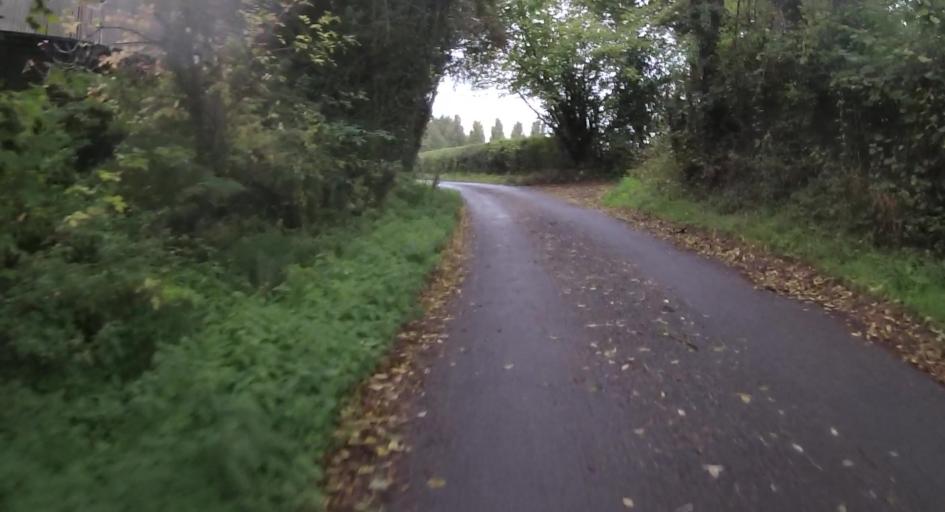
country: GB
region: England
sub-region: Hampshire
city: Tadley
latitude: 51.3491
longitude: -1.1765
